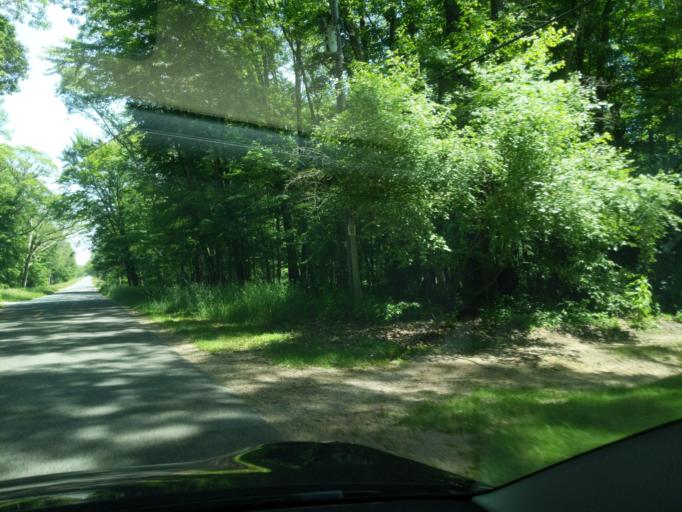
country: US
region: Michigan
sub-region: Muskegon County
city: Montague
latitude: 43.4156
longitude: -86.3876
